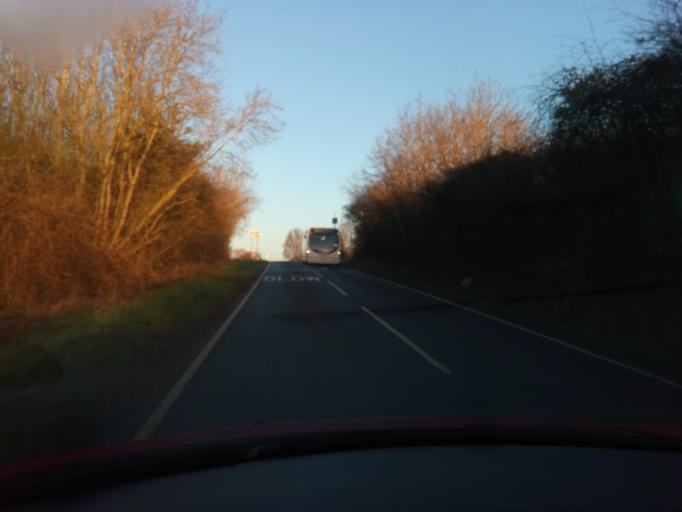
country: GB
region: England
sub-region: Leicestershire
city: Sileby
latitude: 52.7605
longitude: -1.1019
